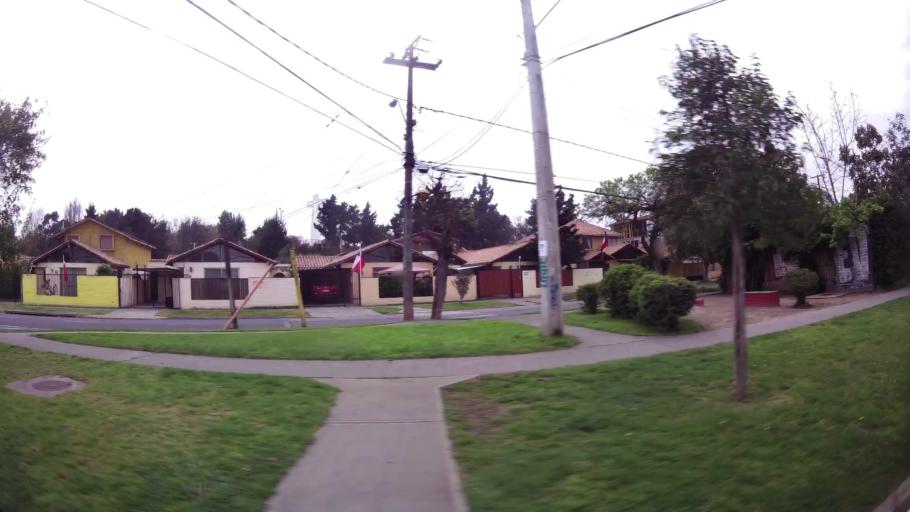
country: CL
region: Santiago Metropolitan
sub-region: Provincia de Santiago
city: Lo Prado
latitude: -33.4962
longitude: -70.7545
